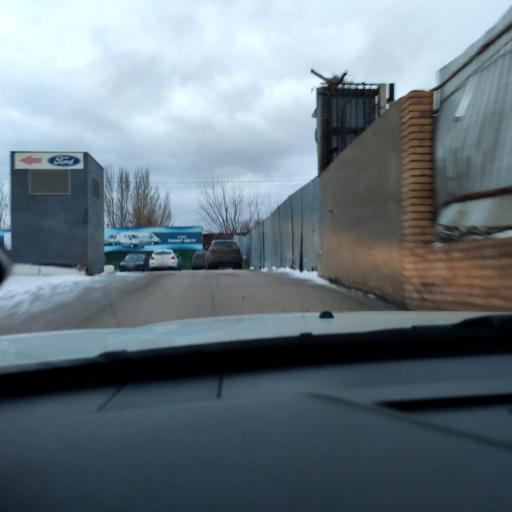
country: RU
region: Samara
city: Samara
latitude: 53.2394
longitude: 50.2449
